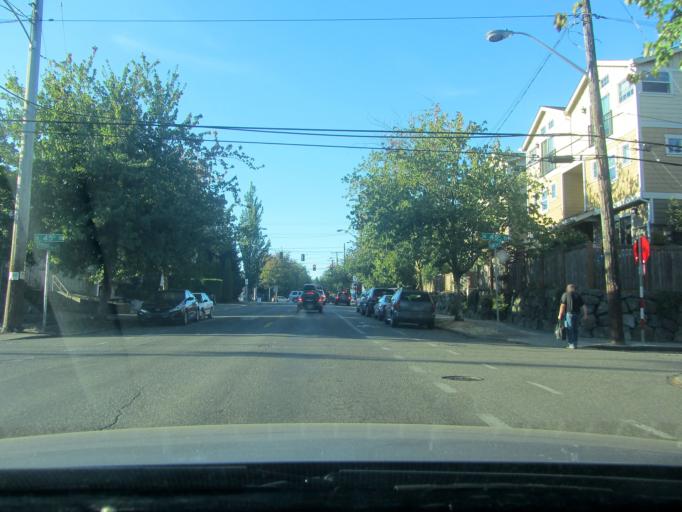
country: US
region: Washington
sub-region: King County
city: Seattle
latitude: 47.6613
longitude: -122.3501
